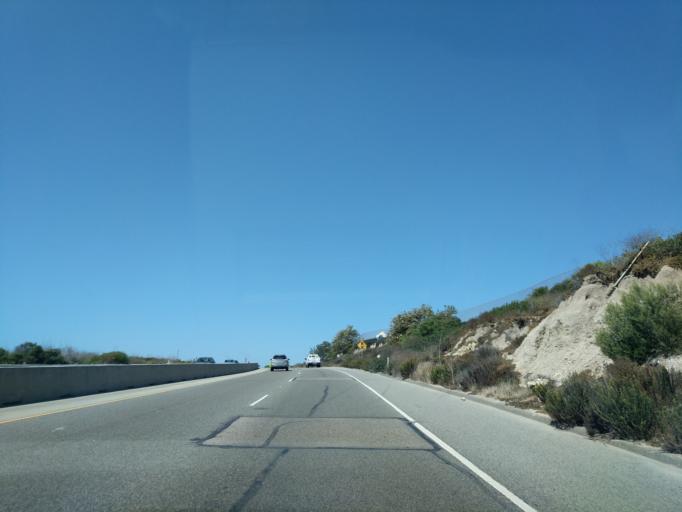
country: US
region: California
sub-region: Orange County
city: Laguna Beach
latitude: 33.5626
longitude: -117.8240
